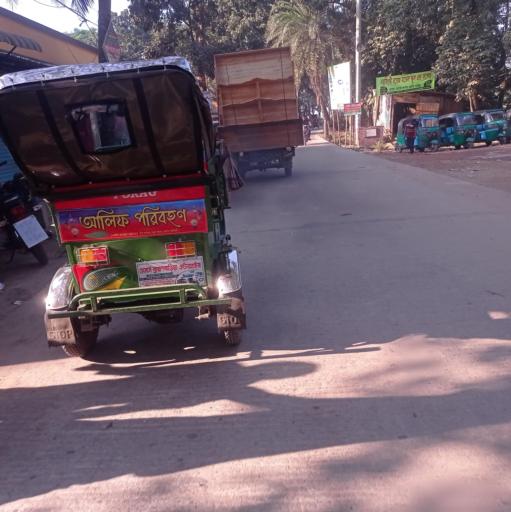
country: BD
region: Dhaka
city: Bhairab Bazar
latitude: 24.1083
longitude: 90.8508
